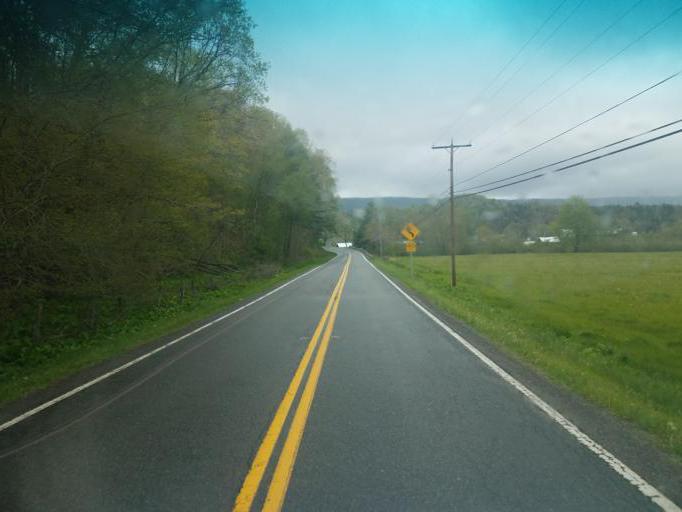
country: US
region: Virginia
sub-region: Bland County
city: Bland
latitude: 37.1695
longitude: -81.1460
